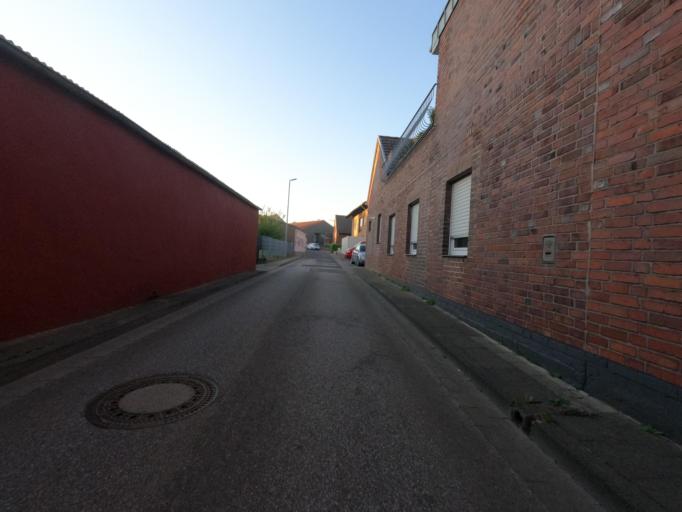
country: DE
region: North Rhine-Westphalia
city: Julich
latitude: 50.9730
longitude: 6.3328
